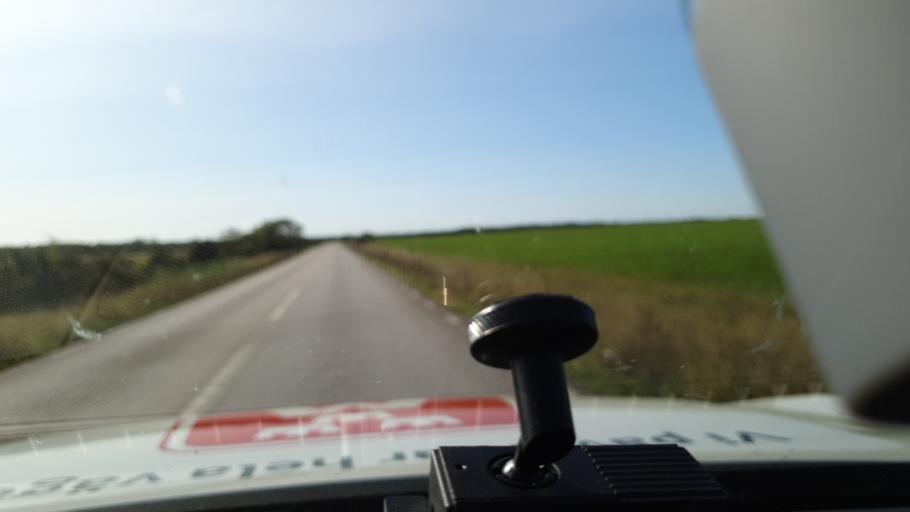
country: SE
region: Gotland
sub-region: Gotland
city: Hemse
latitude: 57.1404
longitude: 18.2845
